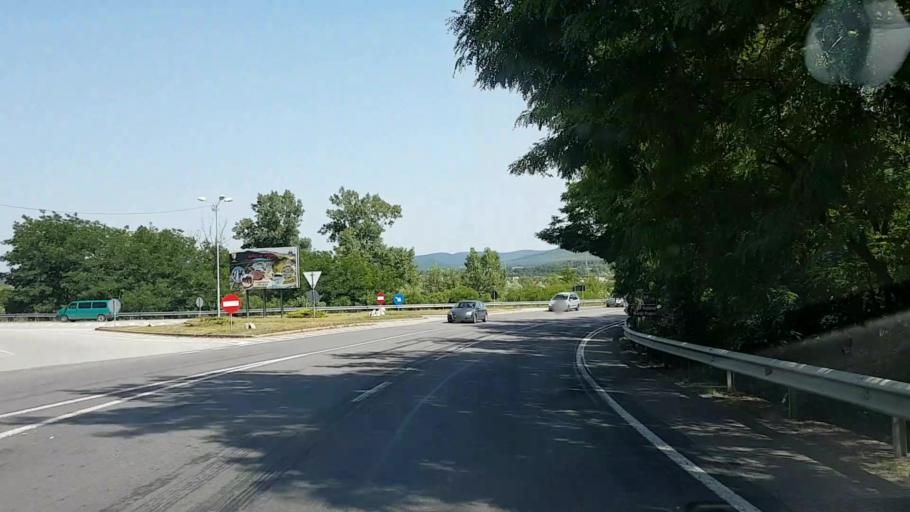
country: RO
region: Bistrita-Nasaud
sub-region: Comuna Beclean
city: Beclean
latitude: 47.1785
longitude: 24.1464
